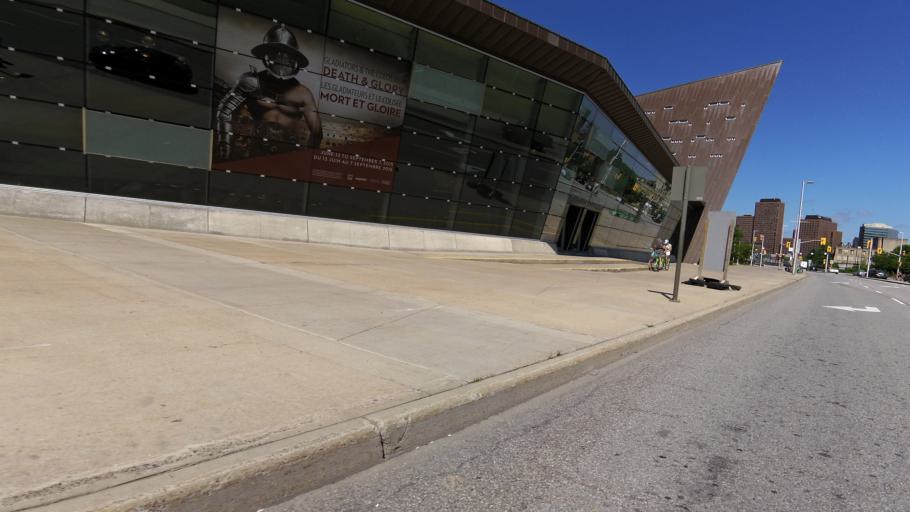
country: CA
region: Ontario
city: Ottawa
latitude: 45.4167
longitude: -75.7151
